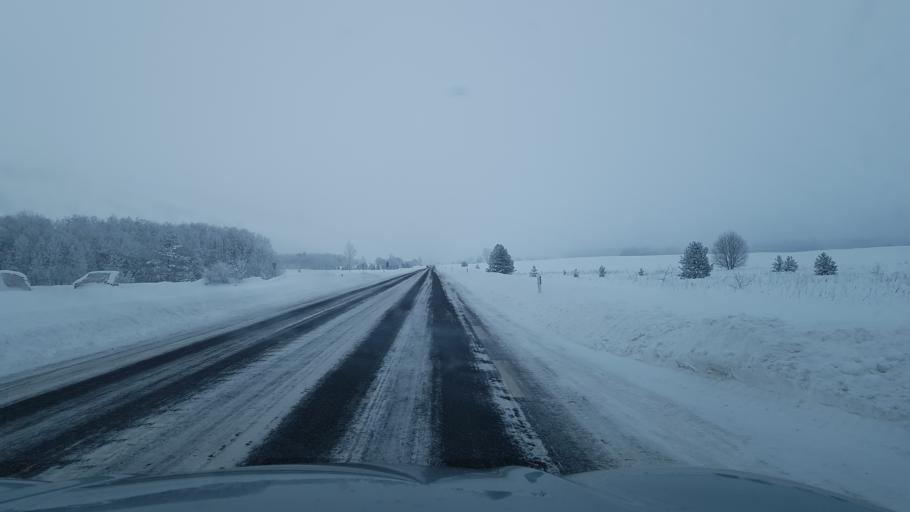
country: EE
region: Ida-Virumaa
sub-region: Johvi vald
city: Johvi
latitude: 59.2415
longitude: 27.3590
